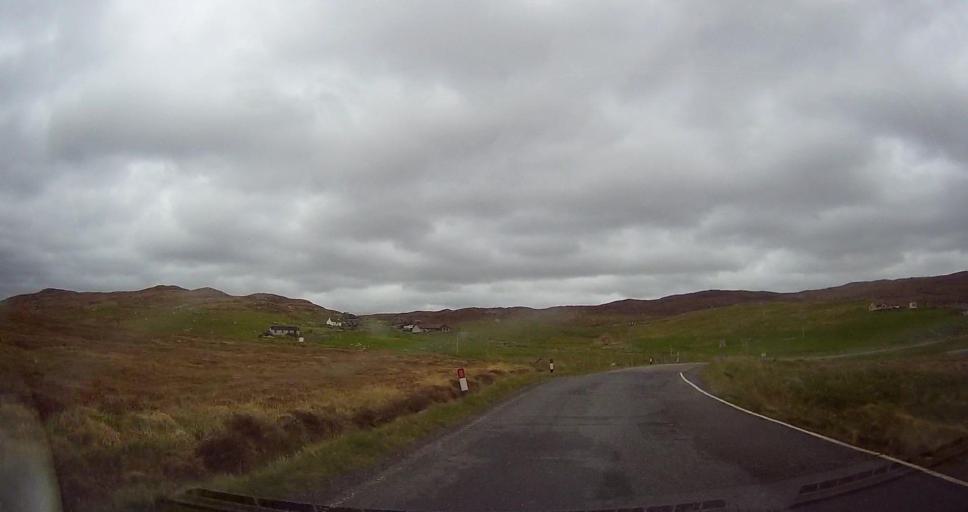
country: GB
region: Scotland
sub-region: Shetland Islands
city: Lerwick
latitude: 60.4921
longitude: -1.4566
